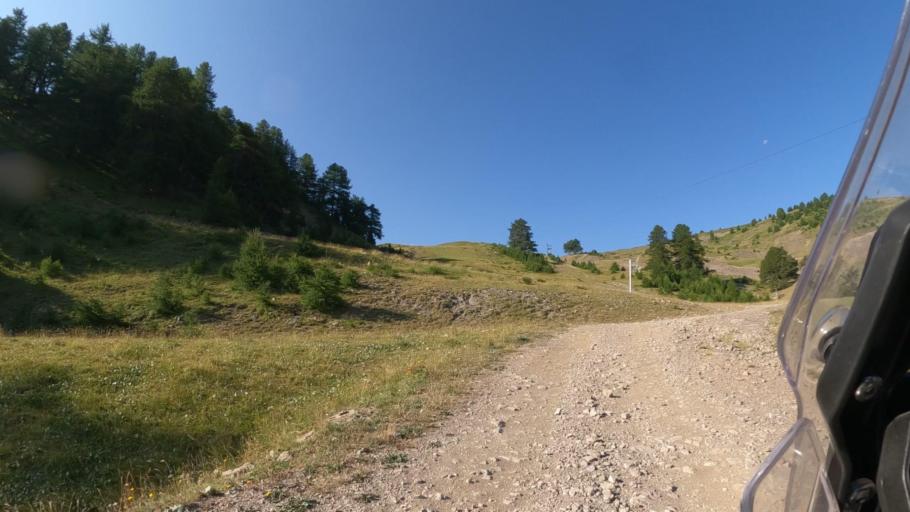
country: FR
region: Provence-Alpes-Cote d'Azur
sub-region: Departement des Hautes-Alpes
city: Guillestre
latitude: 44.6088
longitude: 6.6252
